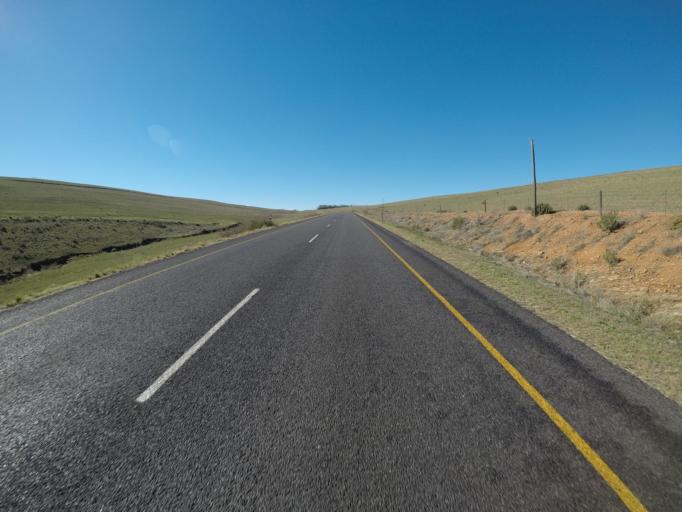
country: ZA
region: Western Cape
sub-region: Overberg District Municipality
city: Caledon
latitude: -34.1458
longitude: 19.4932
